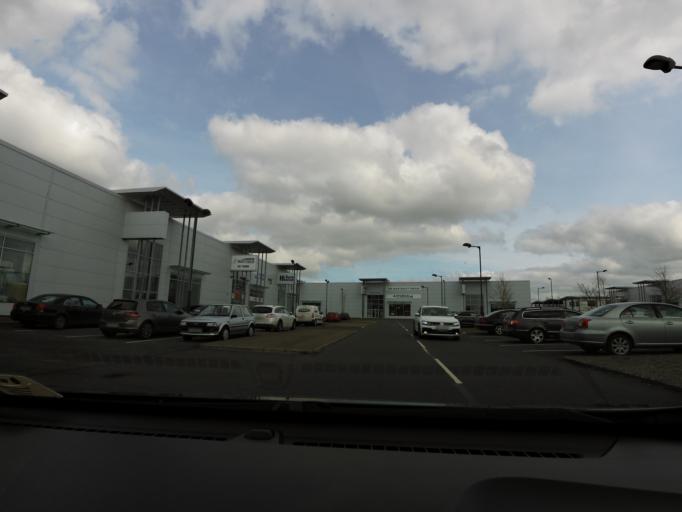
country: IE
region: Connaught
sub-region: County Galway
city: Claregalway
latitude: 53.3341
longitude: -8.9384
